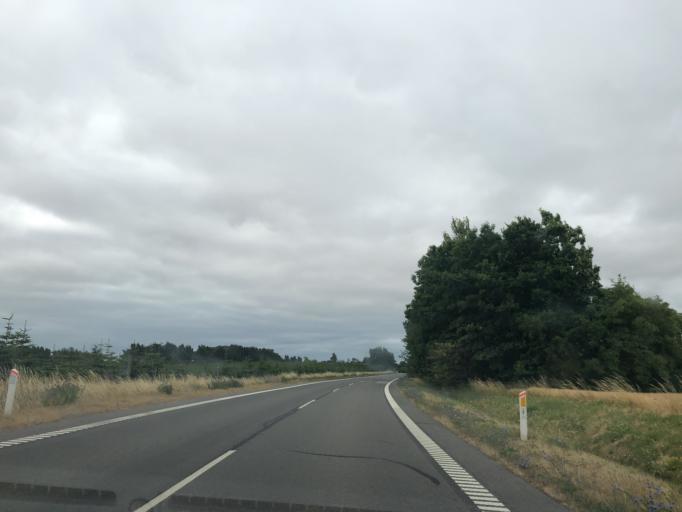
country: DK
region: Zealand
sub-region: Slagelse Kommune
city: Skaelskor
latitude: 55.2586
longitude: 11.3252
